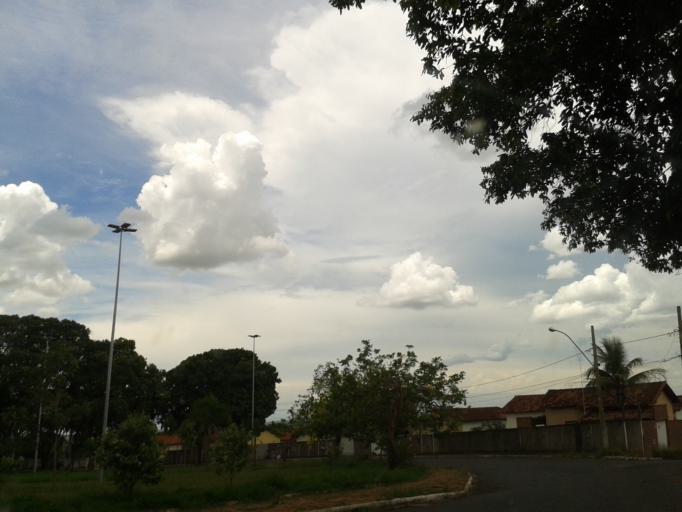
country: BR
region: Minas Gerais
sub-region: Ituiutaba
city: Ituiutaba
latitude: -18.9865
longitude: -49.4531
